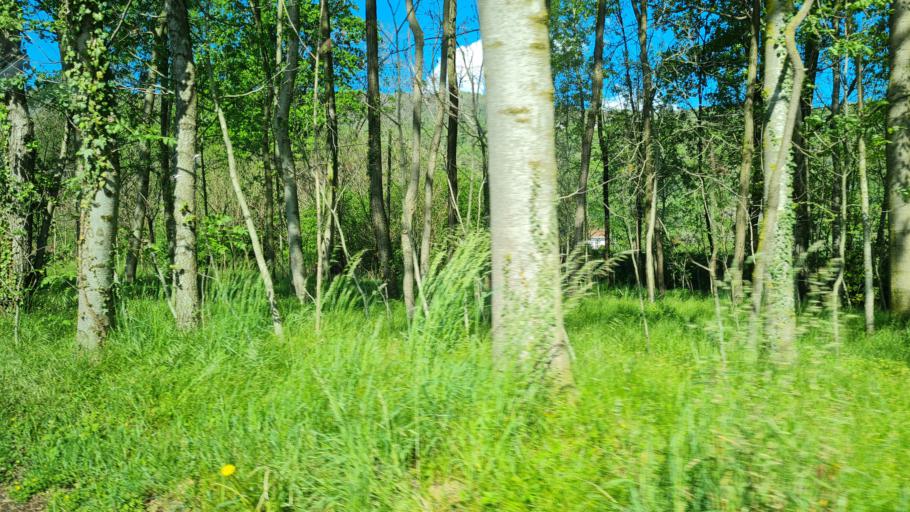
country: IT
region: Piedmont
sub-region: Provincia di Torino
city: Loranze
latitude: 45.4484
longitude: 7.8152
